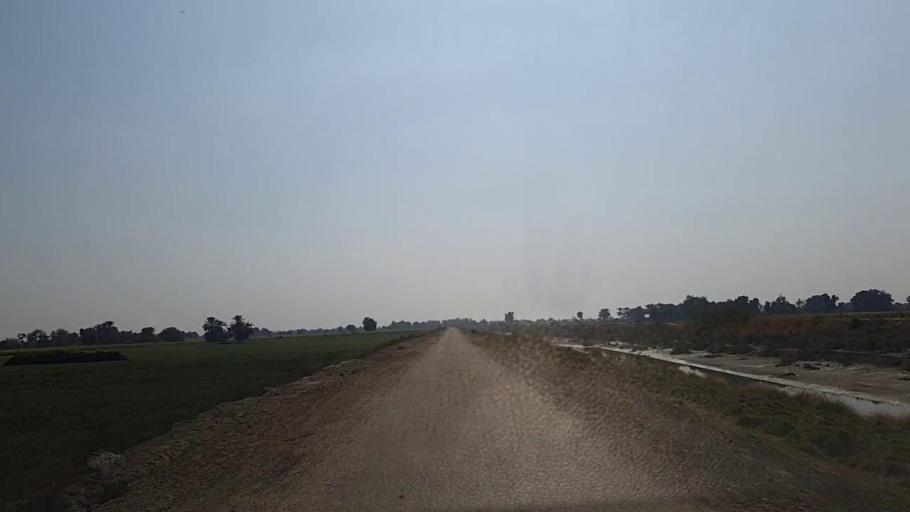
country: PK
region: Sindh
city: Nawabshah
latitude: 26.2583
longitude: 68.5030
